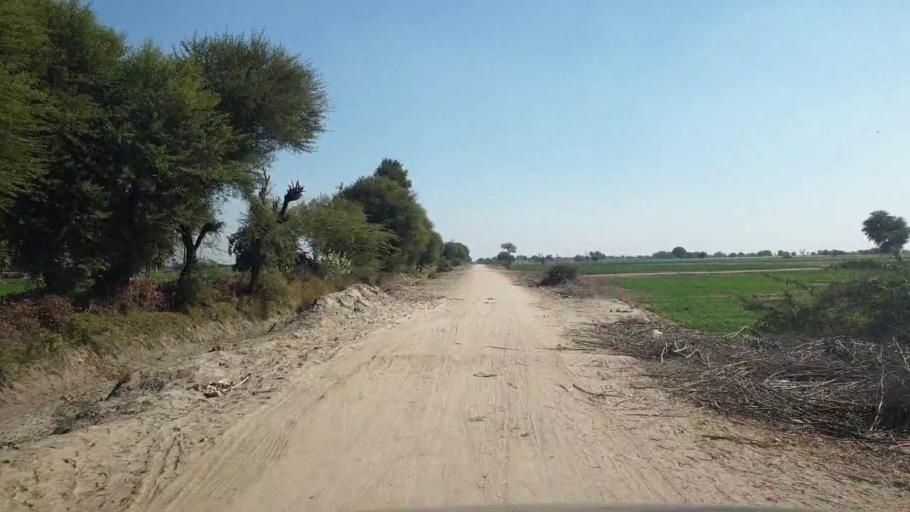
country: PK
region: Sindh
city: Shahpur Chakar
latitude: 26.1401
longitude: 68.6568
